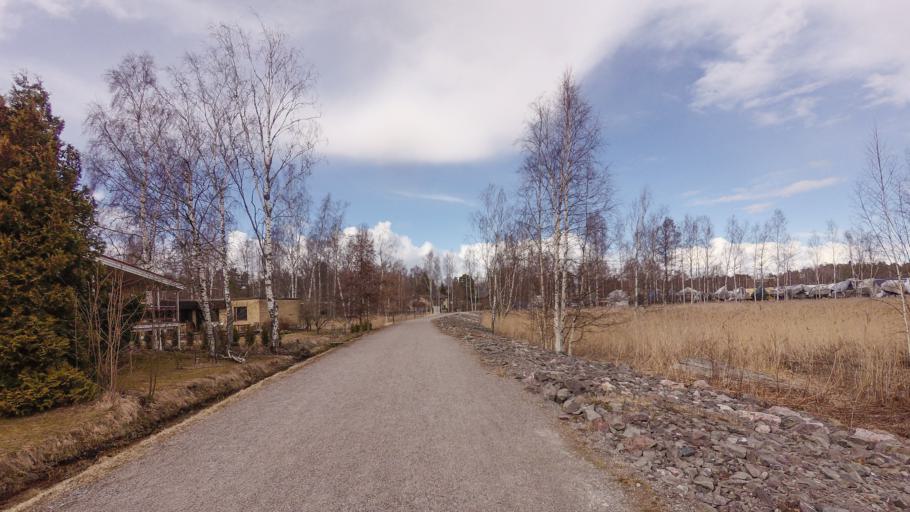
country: FI
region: Uusimaa
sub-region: Helsinki
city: Vantaa
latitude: 60.2043
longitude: 25.0957
